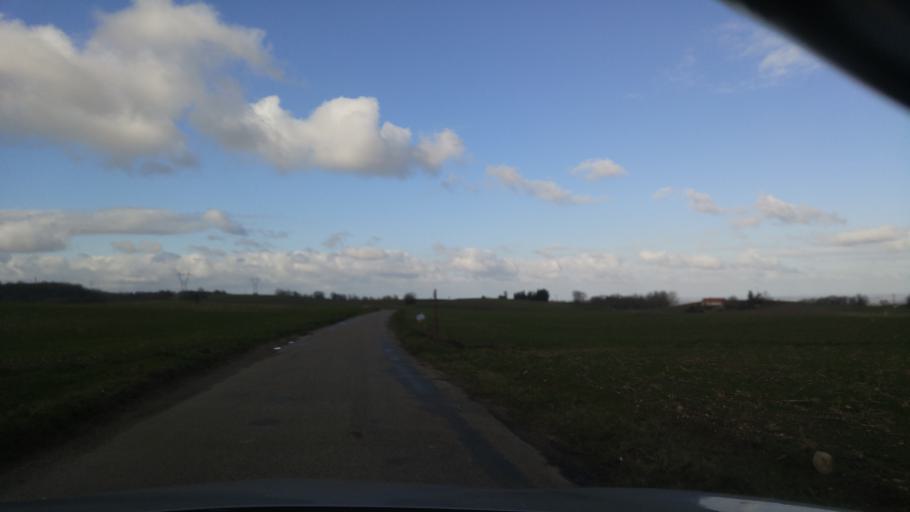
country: FR
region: Rhone-Alpes
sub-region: Departement de l'Isere
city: Roche
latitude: 45.5753
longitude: 5.1780
